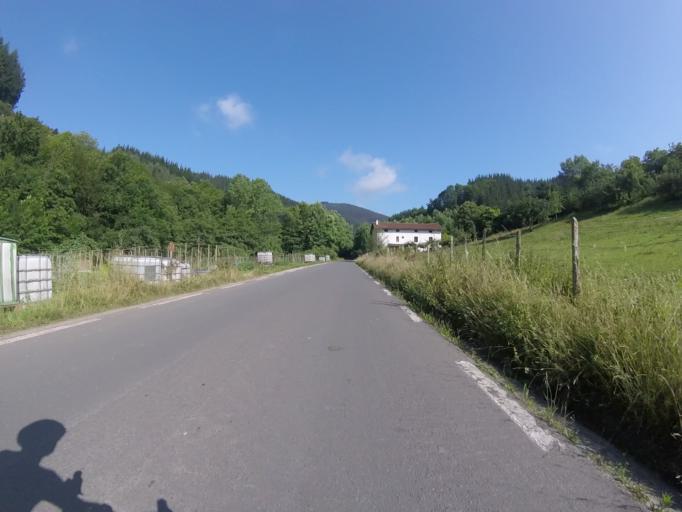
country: ES
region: Basque Country
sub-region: Provincia de Guipuzcoa
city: Ormaiztegui
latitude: 43.0545
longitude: -2.2349
